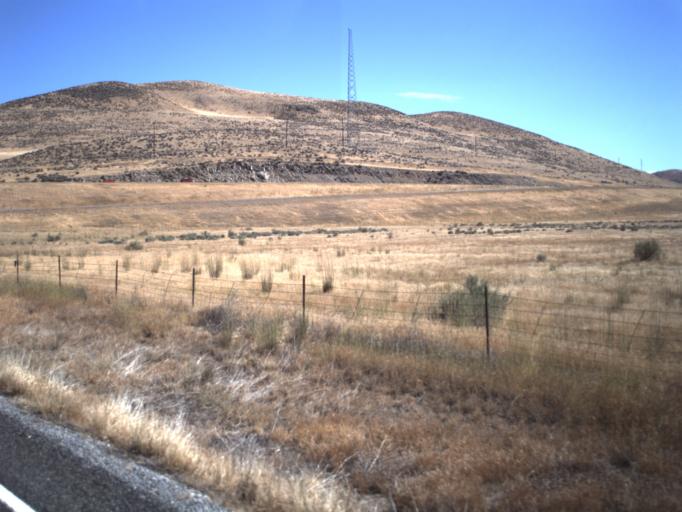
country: US
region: Utah
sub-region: Box Elder County
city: Garland
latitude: 41.8146
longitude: -112.4139
